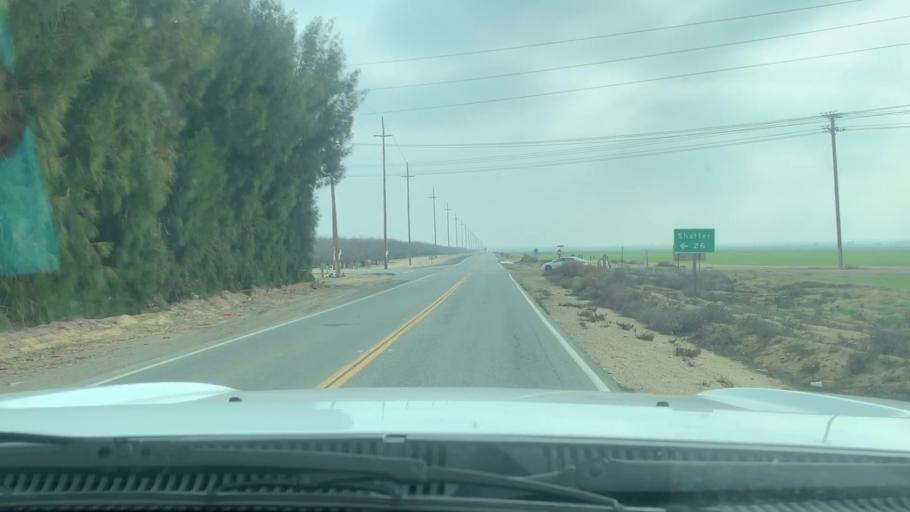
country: US
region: California
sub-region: Kern County
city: Lost Hills
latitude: 35.4996
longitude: -119.7398
